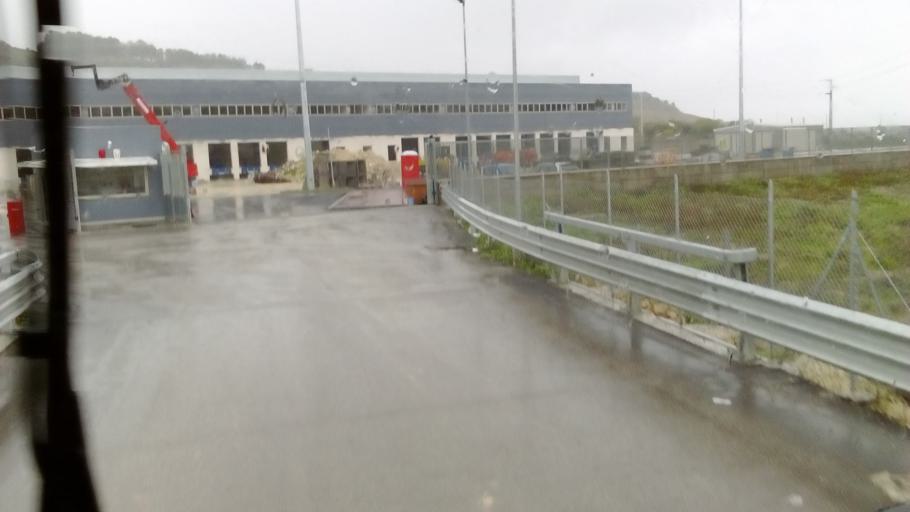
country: IT
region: Sicily
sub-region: Enna
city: Pietraperzia
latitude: 37.4035
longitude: 14.1421
